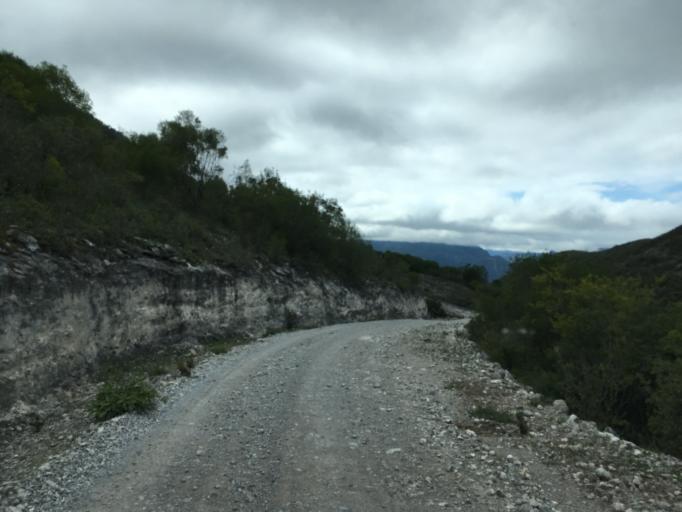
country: MX
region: Hidalgo
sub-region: Metztitlan
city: Fontezuelas
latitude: 20.6226
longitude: -98.8673
